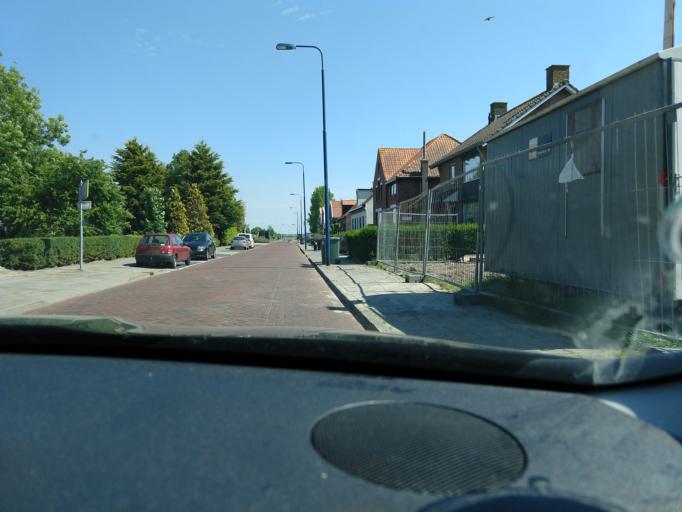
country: NL
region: Zeeland
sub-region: Gemeente Reimerswaal
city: Yerseke
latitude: 51.5849
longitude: 4.0170
